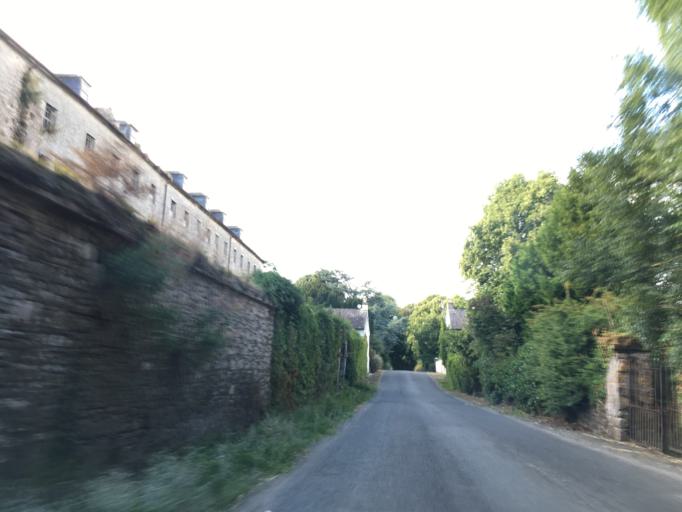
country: IE
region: Munster
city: Cahir
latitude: 52.2806
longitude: -7.9534
